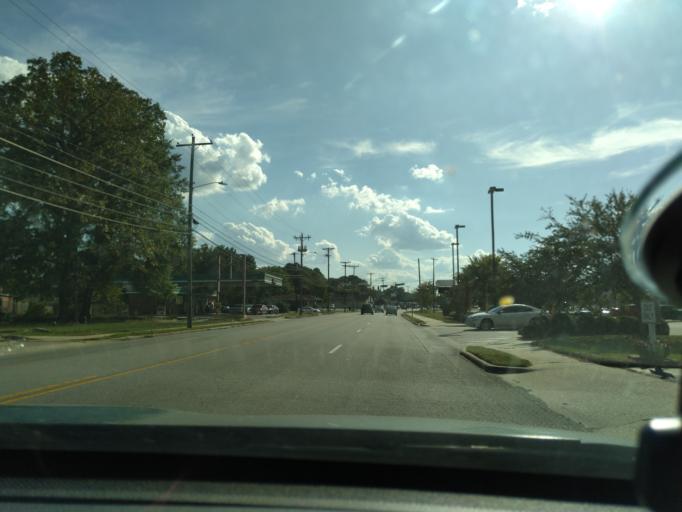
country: US
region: North Carolina
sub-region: Nash County
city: Rocky Mount
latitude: 35.9339
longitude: -77.8097
